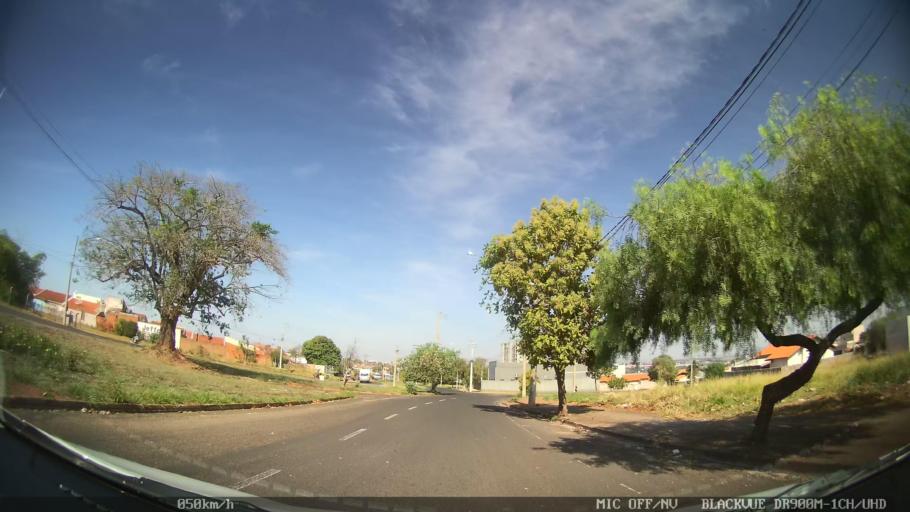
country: BR
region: Sao Paulo
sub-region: Sao Jose Do Rio Preto
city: Sao Jose do Rio Preto
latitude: -20.7873
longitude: -49.4241
